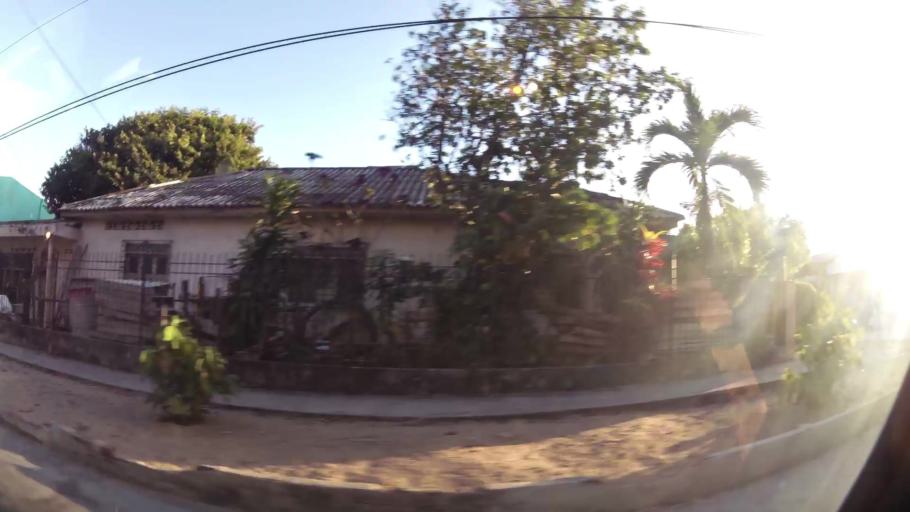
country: CO
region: Atlantico
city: Barranquilla
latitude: 10.9699
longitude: -74.8041
